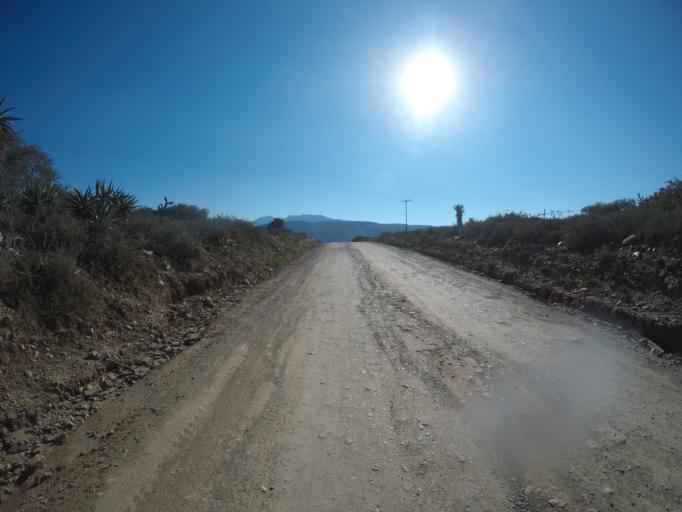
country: ZA
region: Eastern Cape
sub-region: Cacadu District Municipality
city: Kruisfontein
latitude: -33.6725
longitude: 24.5765
